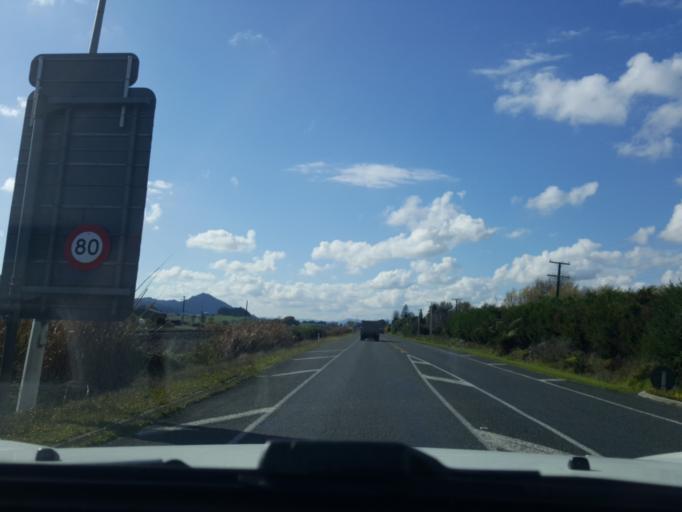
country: NZ
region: Waikato
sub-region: Waikato District
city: Ngaruawahia
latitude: -37.6565
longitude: 175.1533
